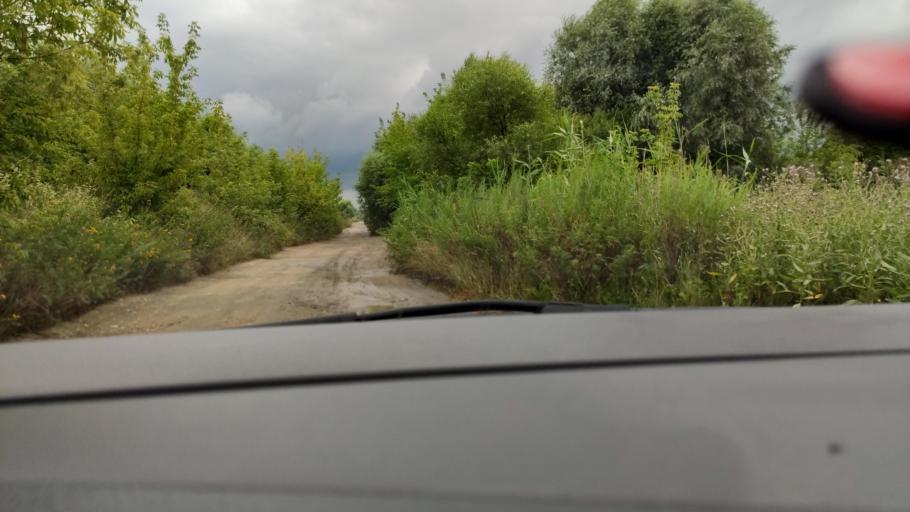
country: RU
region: Voronezj
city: Ramon'
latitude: 51.9040
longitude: 39.3521
